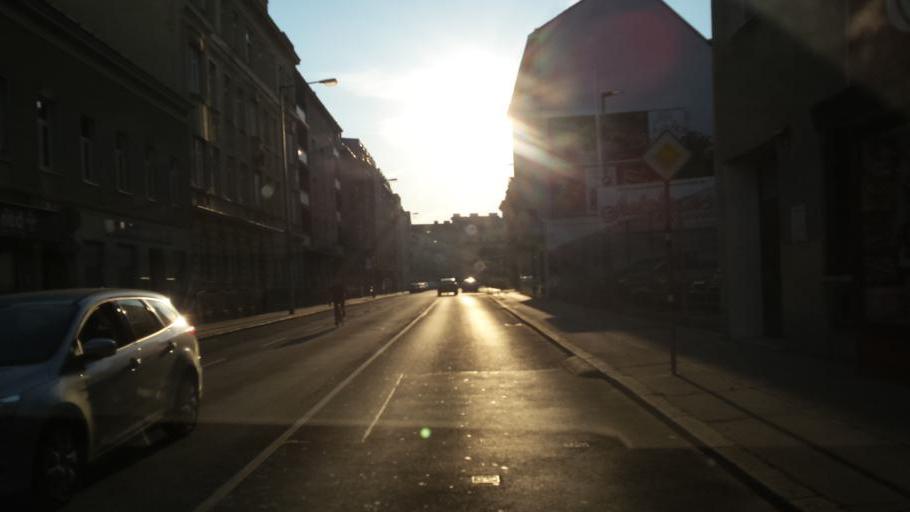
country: AT
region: Vienna
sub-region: Wien Stadt
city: Vienna
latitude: 48.2601
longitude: 16.3989
